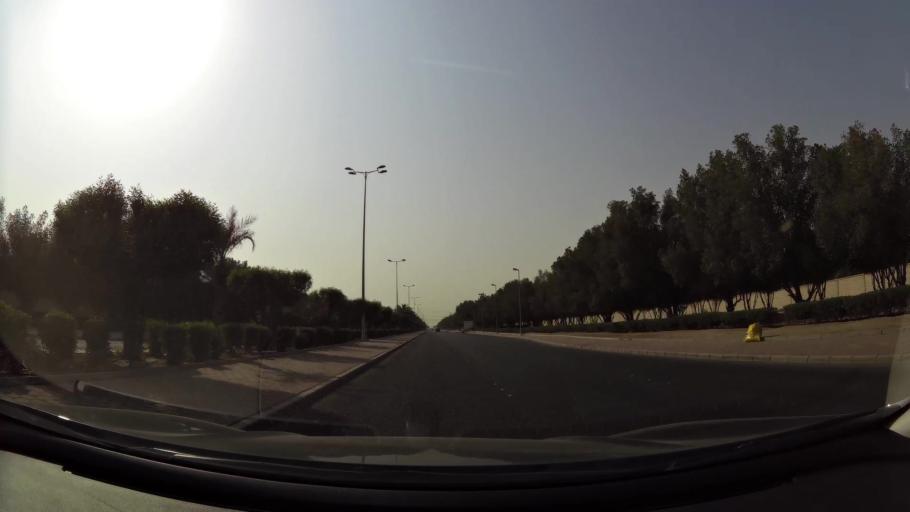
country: KW
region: Al Asimah
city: Ar Rabiyah
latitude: 29.3047
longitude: 47.8321
